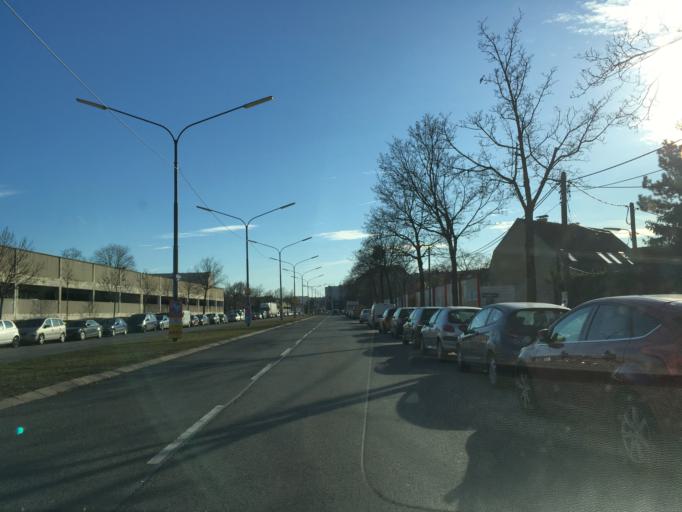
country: AT
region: Lower Austria
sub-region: Politischer Bezirk Wien-Umgebung
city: Gerasdorf bei Wien
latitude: 48.2590
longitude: 16.4385
